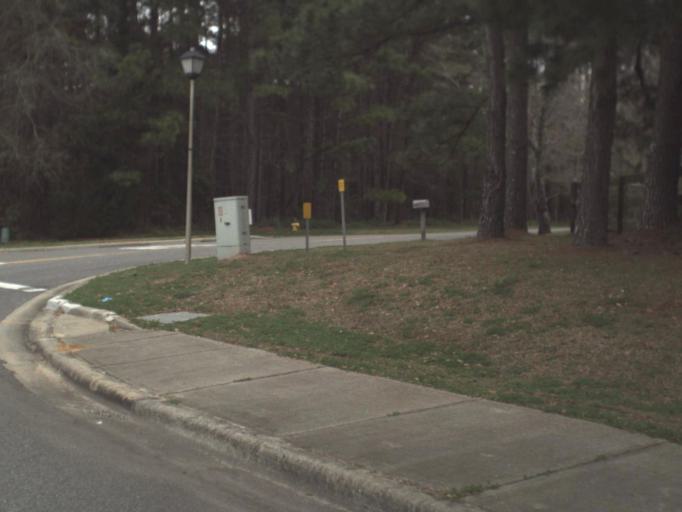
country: US
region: Florida
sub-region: Leon County
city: Tallahassee
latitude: 30.5571
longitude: -84.2204
